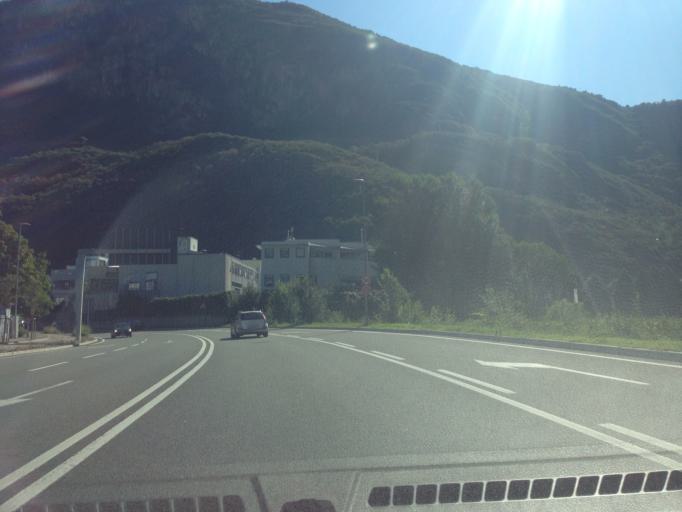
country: IT
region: Trentino-Alto Adige
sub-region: Bolzano
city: San Giacomo
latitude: 46.4681
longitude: 11.3298
